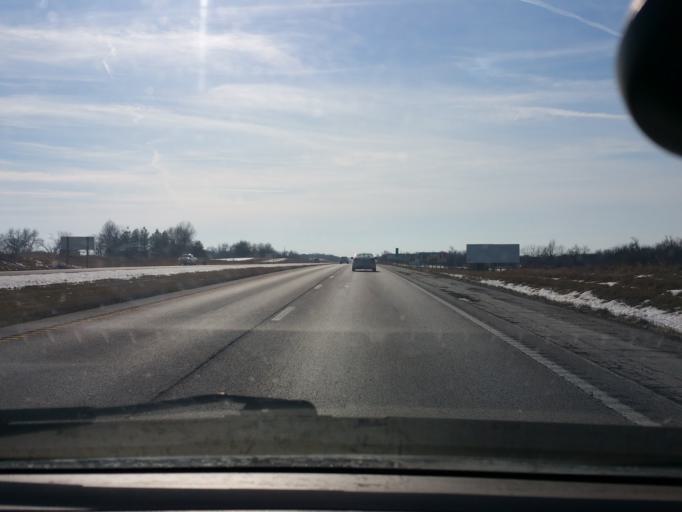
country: US
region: Missouri
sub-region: Clinton County
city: Cameron
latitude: 39.7201
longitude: -94.2227
